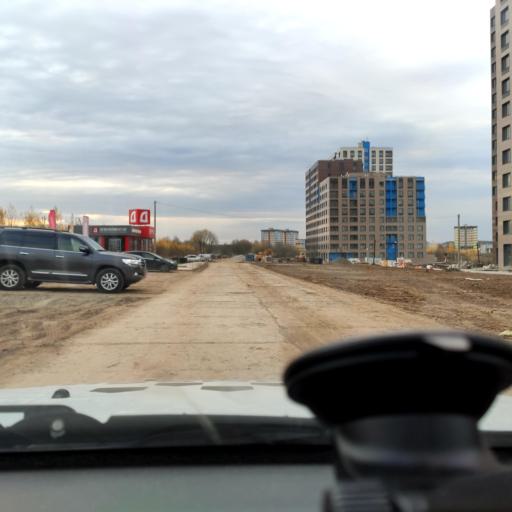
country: RU
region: Perm
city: Perm
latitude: 58.0106
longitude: 56.3327
